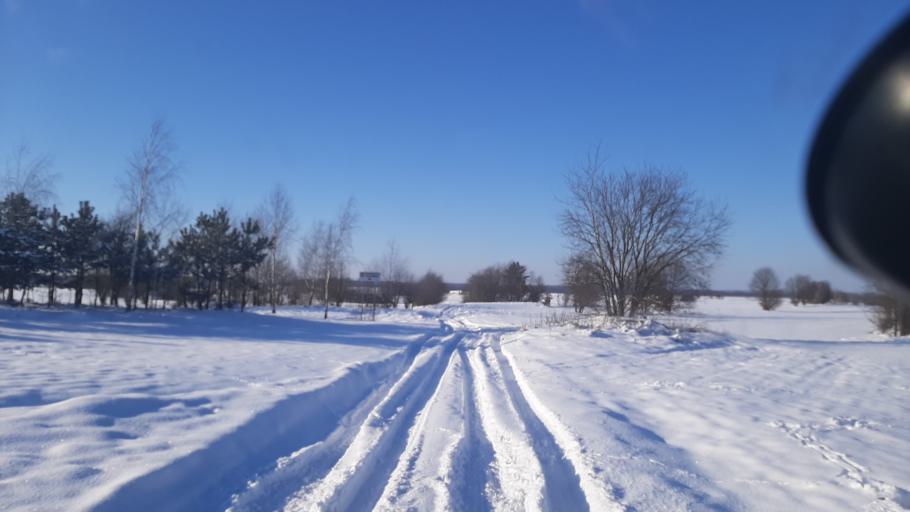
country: PL
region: Lublin Voivodeship
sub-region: Powiat lubelski
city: Jastkow
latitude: 51.3777
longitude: 22.4357
